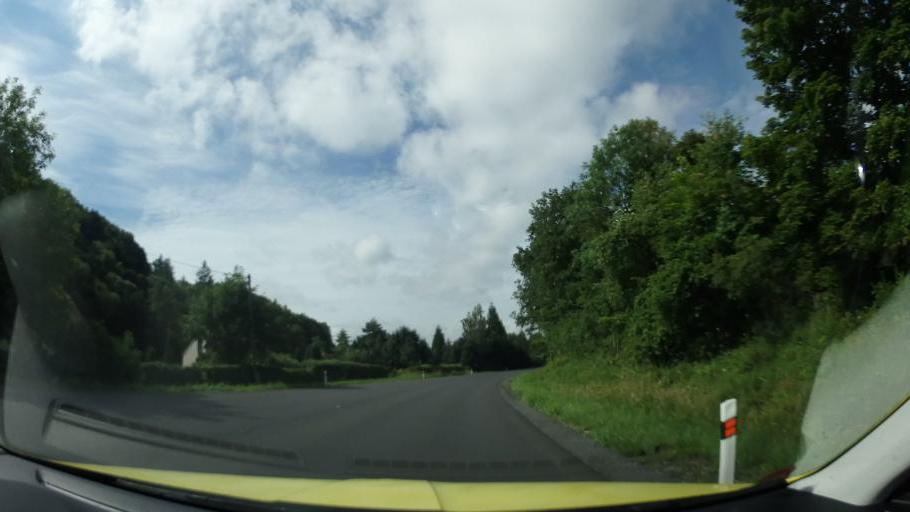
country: CZ
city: Hodslavice
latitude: 49.5606
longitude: 18.0258
